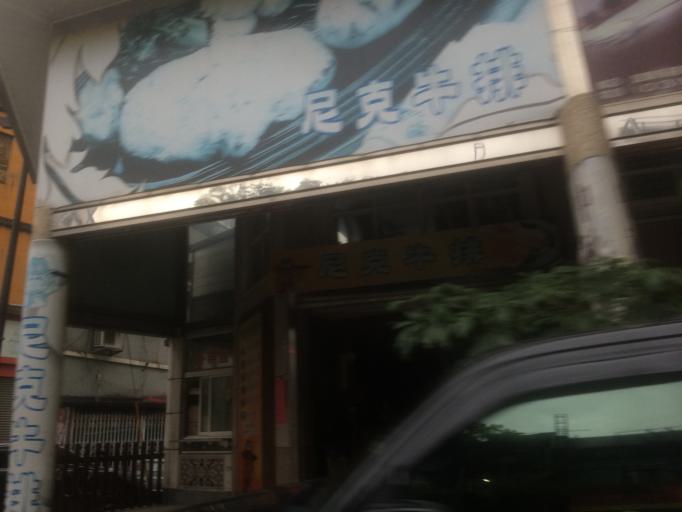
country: TW
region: Taiwan
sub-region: Yilan
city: Yilan
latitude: 24.6744
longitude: 121.7640
